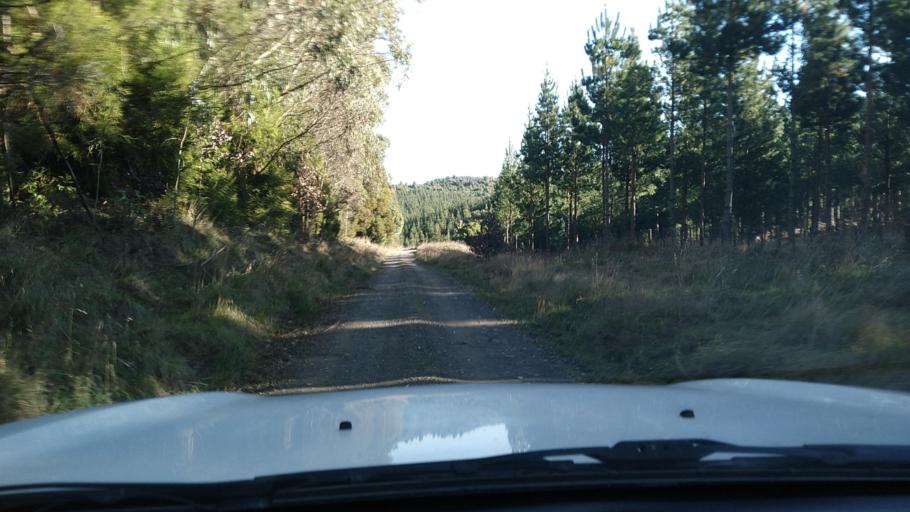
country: NZ
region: Waikato
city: Turangi
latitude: -38.6471
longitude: 175.7017
